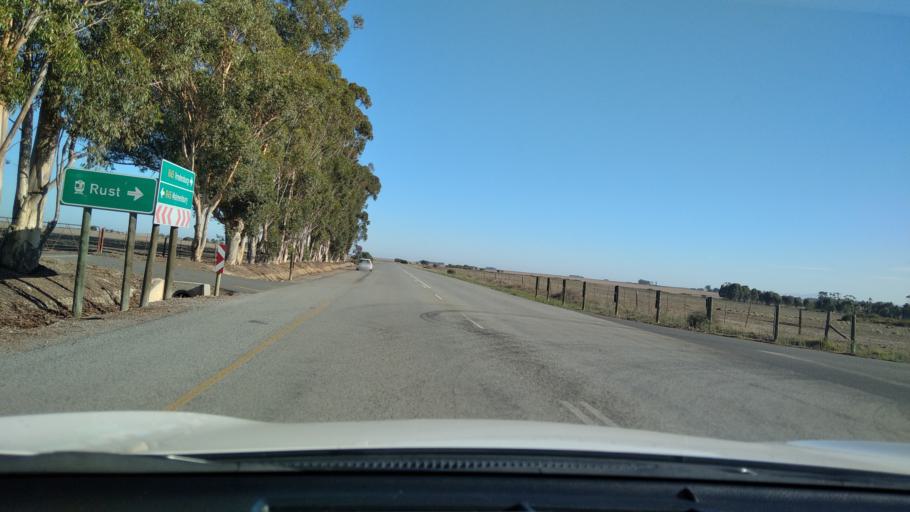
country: ZA
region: Western Cape
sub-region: West Coast District Municipality
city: Moorreesburg
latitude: -33.2615
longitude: 18.5937
